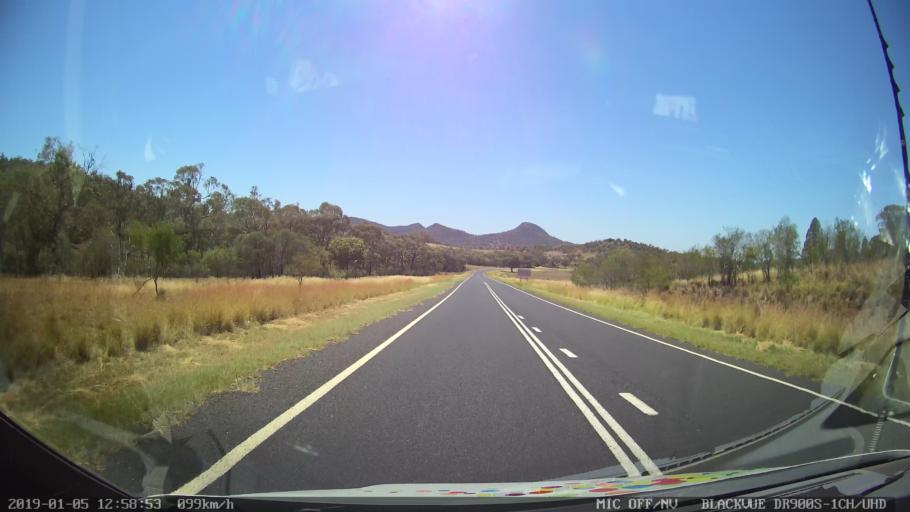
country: AU
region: New South Wales
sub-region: Narrabri
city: Boggabri
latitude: -31.1131
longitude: 149.7568
